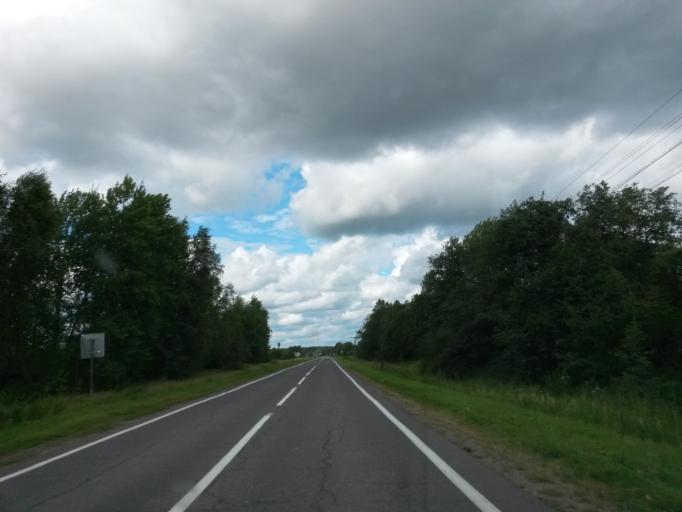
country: RU
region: Jaroslavl
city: Tutayev
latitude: 57.9304
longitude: 39.5039
